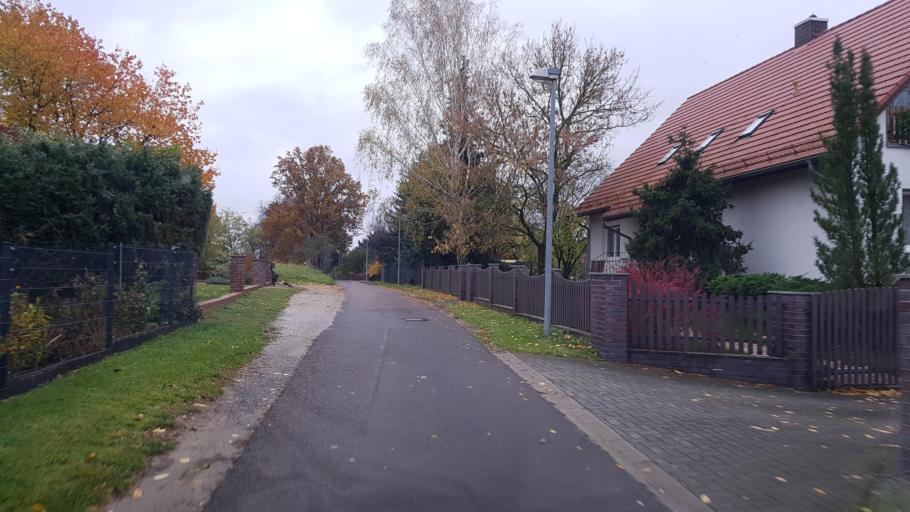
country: DE
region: Brandenburg
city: Drebkau
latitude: 51.6981
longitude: 14.2451
